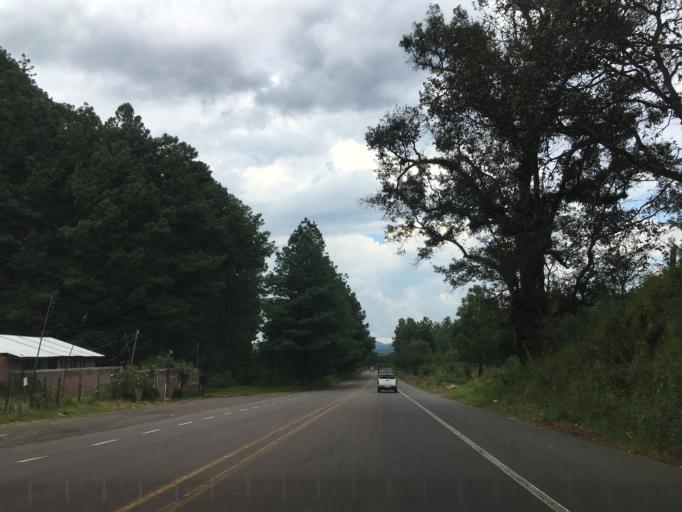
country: MX
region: Michoacan
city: Angahuan
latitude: 19.5285
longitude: -102.1914
